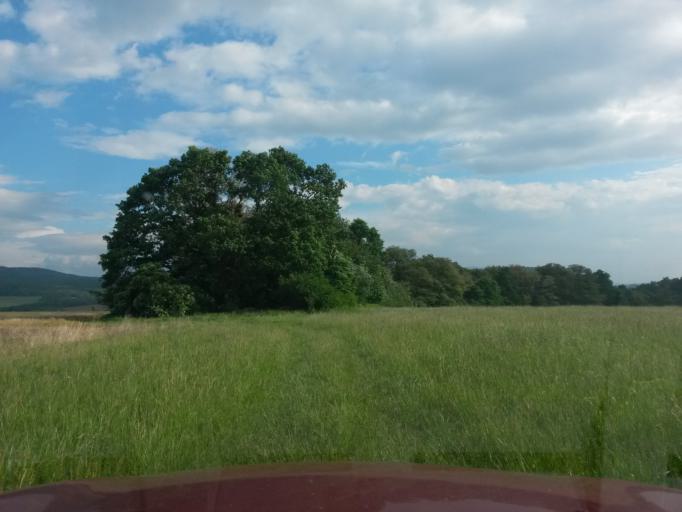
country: SK
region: Kosicky
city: Kosice
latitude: 48.7386
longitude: 21.4586
